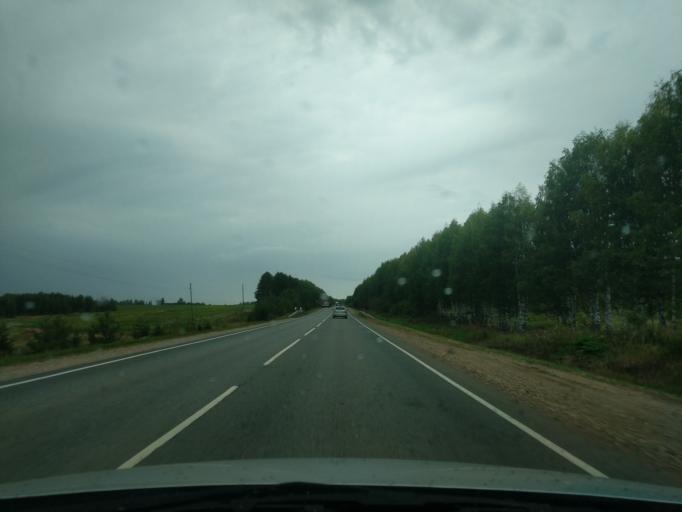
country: RU
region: Kirov
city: Orlov
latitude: 58.5466
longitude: 48.8732
